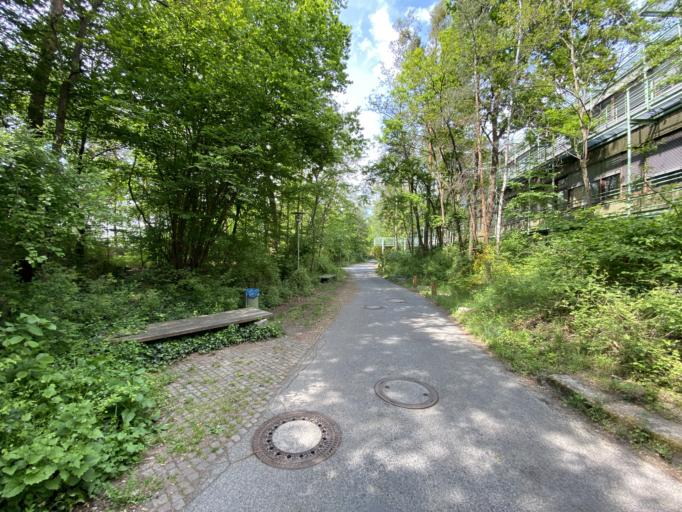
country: DE
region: Bavaria
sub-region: Regierungsbezirk Mittelfranken
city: Erlangen
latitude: 49.5791
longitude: 11.0285
